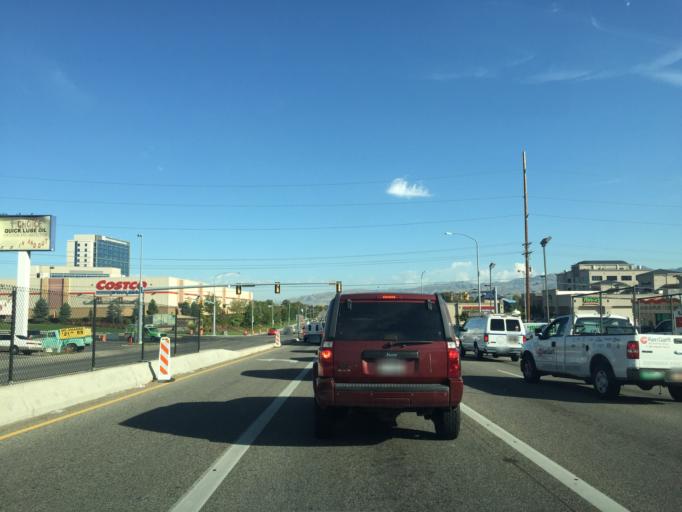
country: US
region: Utah
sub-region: Salt Lake County
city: Murray
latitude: 40.6552
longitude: -111.8883
